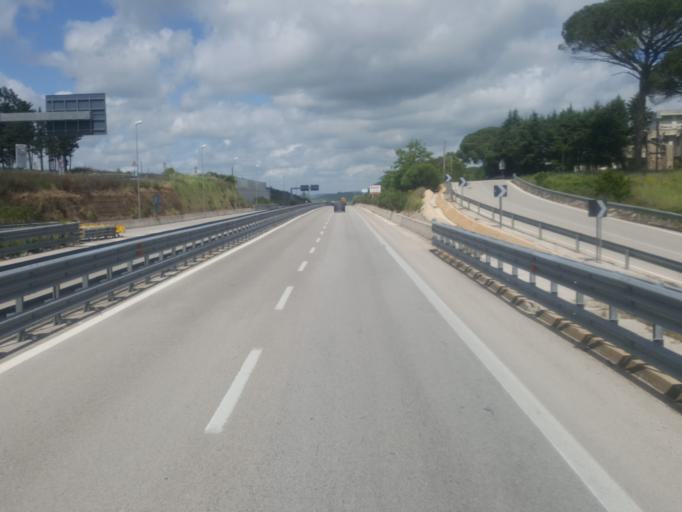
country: IT
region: Basilicate
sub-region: Provincia di Matera
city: Matera
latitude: 40.7013
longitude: 16.5869
